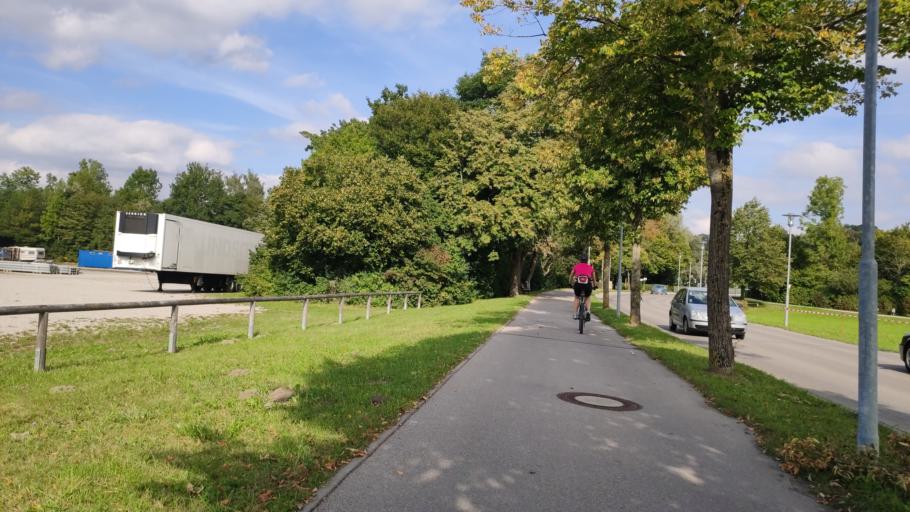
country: DE
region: Bavaria
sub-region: Upper Bavaria
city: Kaufering
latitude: 48.0901
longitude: 10.8716
